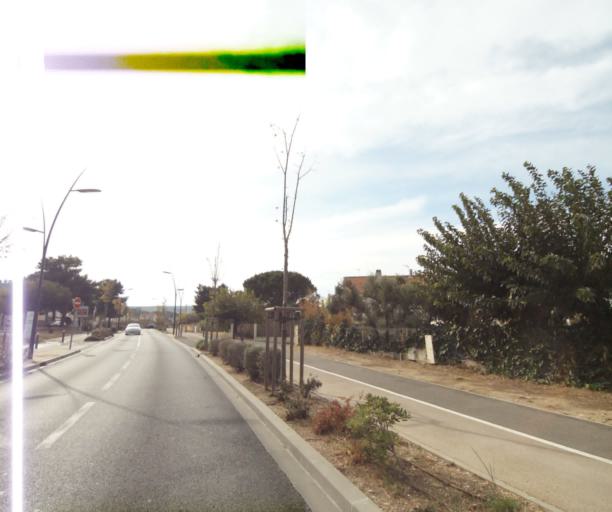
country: FR
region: Provence-Alpes-Cote d'Azur
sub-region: Departement des Bouches-du-Rhone
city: Gignac-la-Nerthe
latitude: 43.3900
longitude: 5.2316
